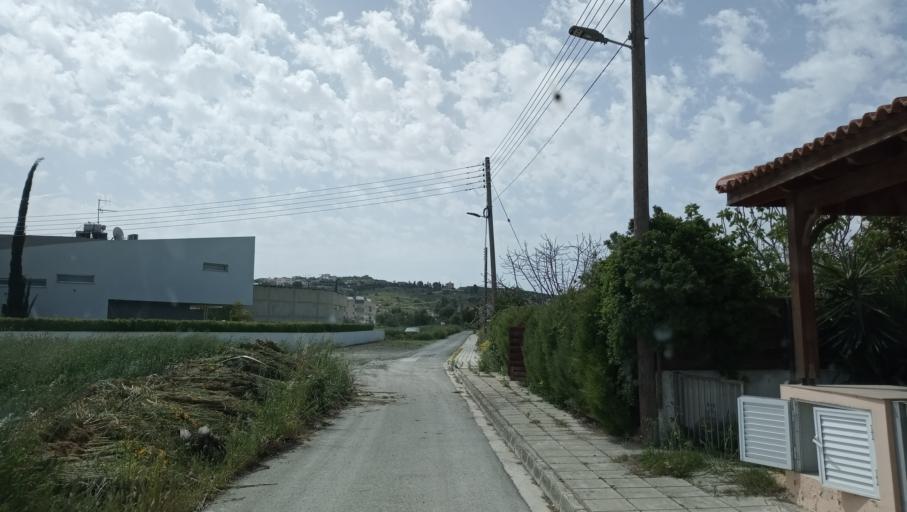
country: CY
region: Lefkosia
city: Dali
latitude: 35.0234
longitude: 33.4317
